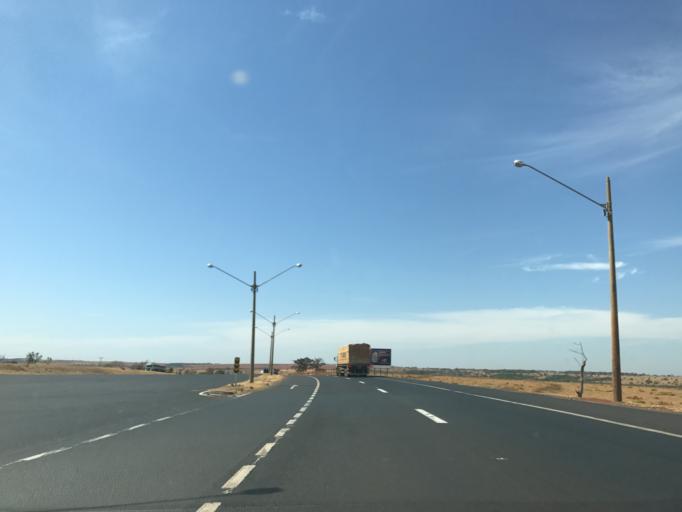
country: BR
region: Minas Gerais
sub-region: Monte Alegre De Minas
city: Monte Alegre de Minas
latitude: -18.8679
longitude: -49.0671
